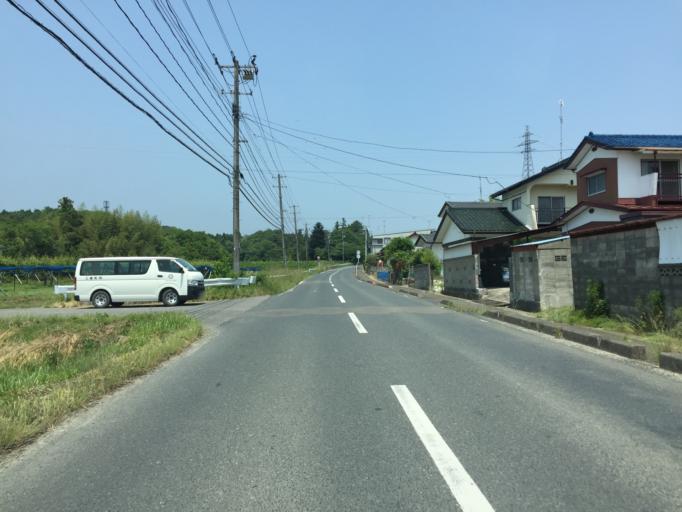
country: JP
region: Miyagi
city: Marumori
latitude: 37.8171
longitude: 140.8973
